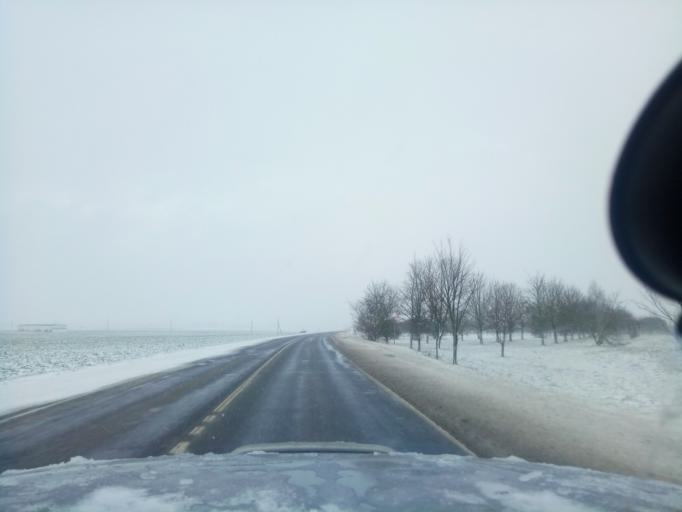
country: BY
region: Minsk
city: Haradzyeya
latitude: 53.3191
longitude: 26.5592
